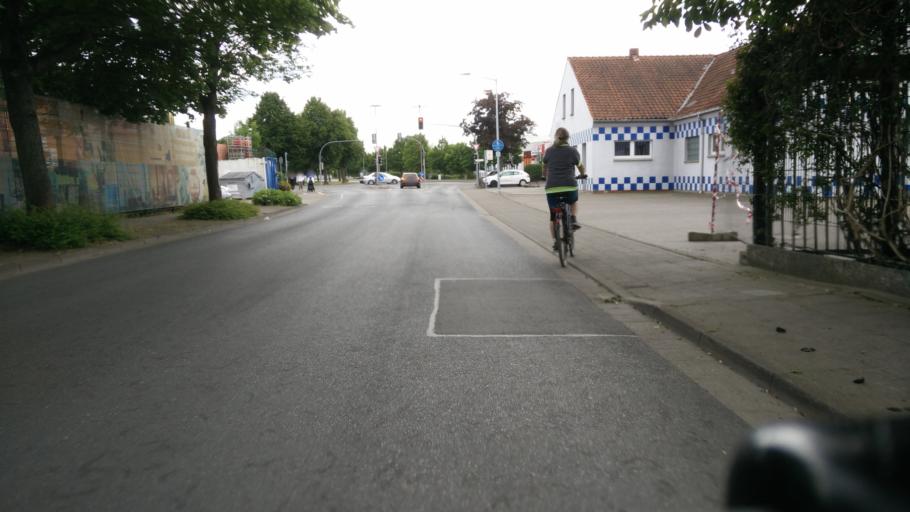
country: DE
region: Lower Saxony
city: Wunstorf
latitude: 52.4294
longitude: 9.4151
